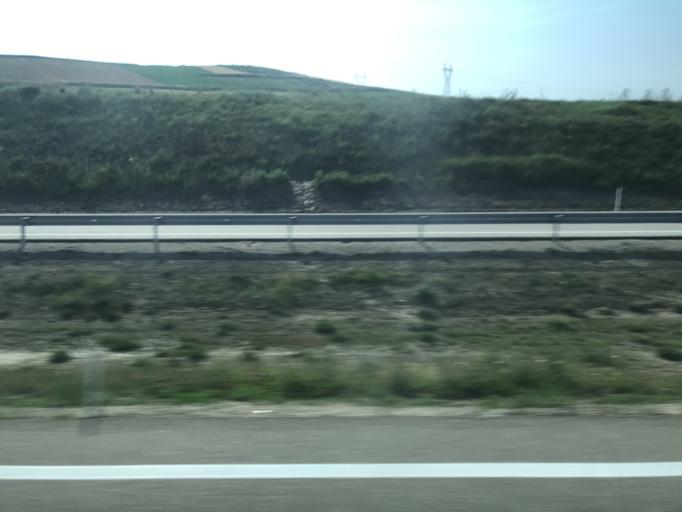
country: ES
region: Castille and Leon
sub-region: Provincia de Burgos
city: Rubena
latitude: 42.3736
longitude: -3.5882
